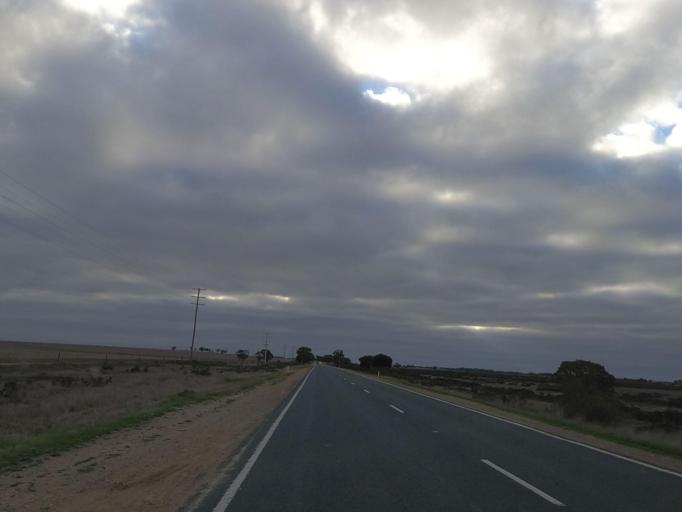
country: AU
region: Victoria
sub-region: Swan Hill
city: Swan Hill
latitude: -35.6382
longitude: 143.8259
